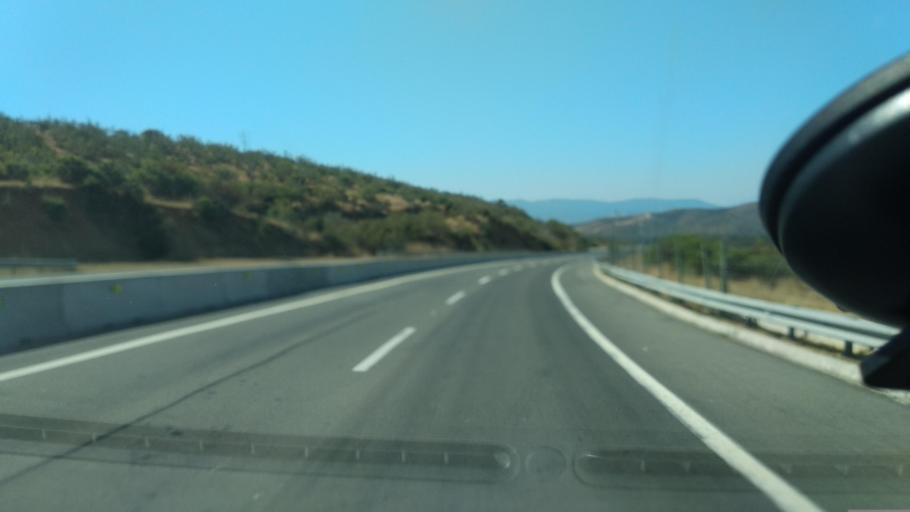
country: CL
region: Valparaiso
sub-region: Provincia de Marga Marga
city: Villa Alemana
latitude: -33.0376
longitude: -71.3195
